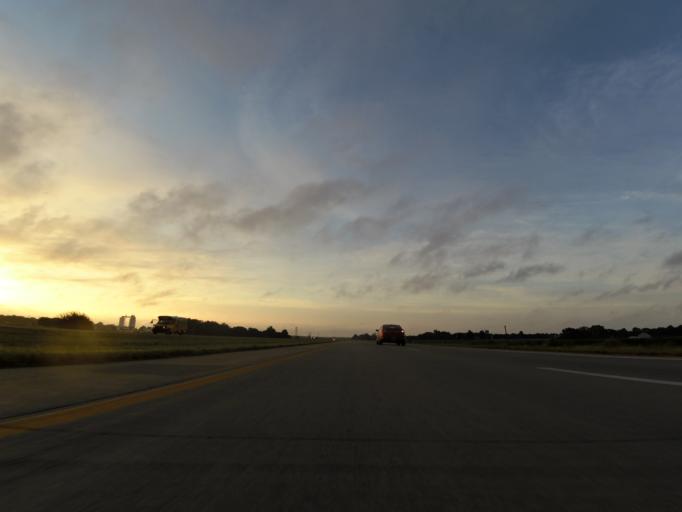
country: US
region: Kansas
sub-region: Reno County
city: Haven
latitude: 37.9030
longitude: -97.7966
